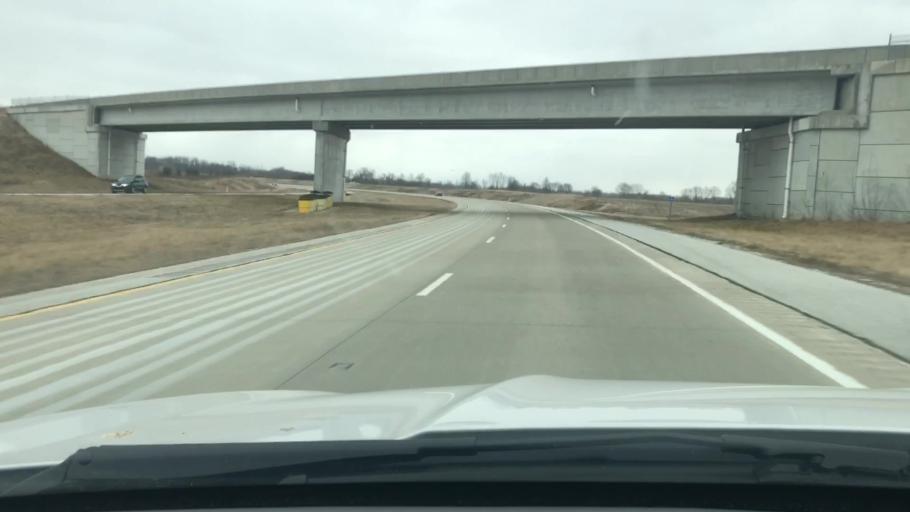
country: US
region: Indiana
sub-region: Carroll County
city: Delphi
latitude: 40.5236
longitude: -86.7149
